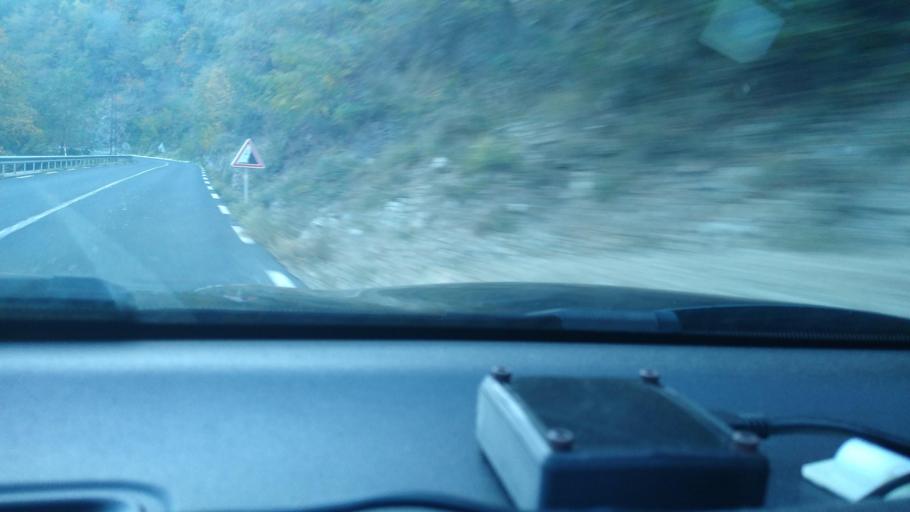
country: ES
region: Catalonia
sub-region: Provincia de Girona
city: Llivia
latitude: 42.5115
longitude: 2.1772
